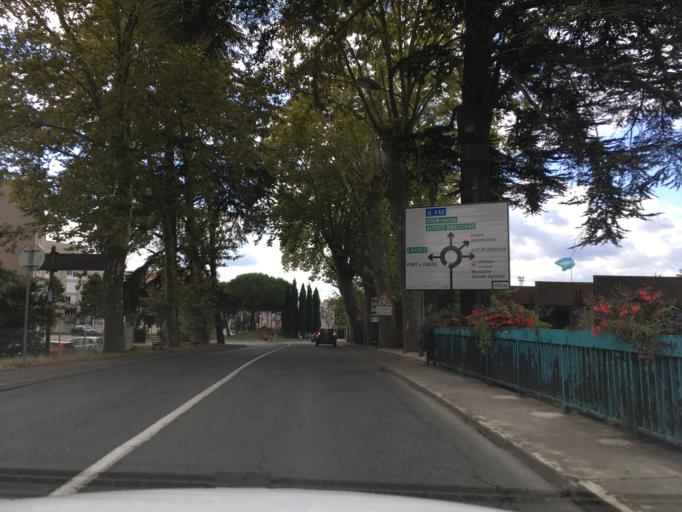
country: FR
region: Aquitaine
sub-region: Departement du Lot-et-Garonne
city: Agen
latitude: 44.2097
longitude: 0.6288
